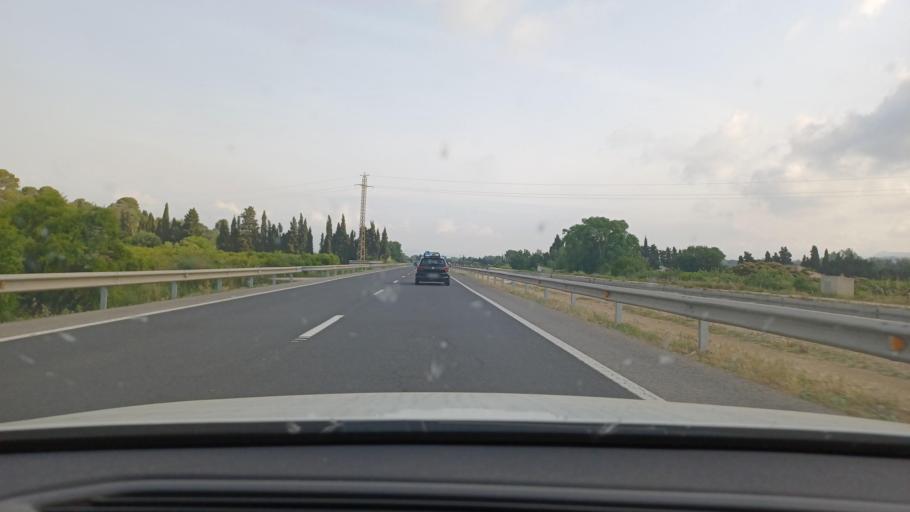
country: ES
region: Catalonia
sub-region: Provincia de Tarragona
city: Masdenverge
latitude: 40.7647
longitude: 0.5325
